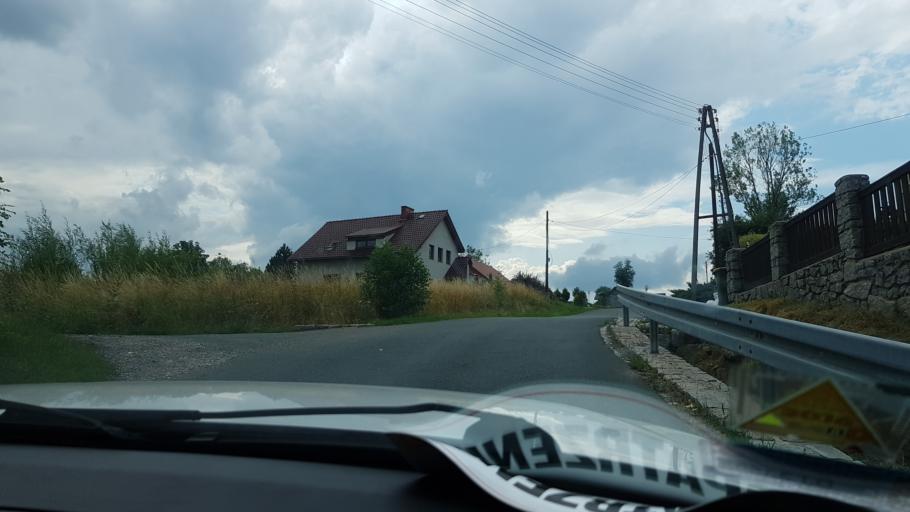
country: PL
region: Lower Silesian Voivodeship
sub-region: Powiat jeleniogorski
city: Jezow Sudecki
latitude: 50.9356
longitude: 15.7925
